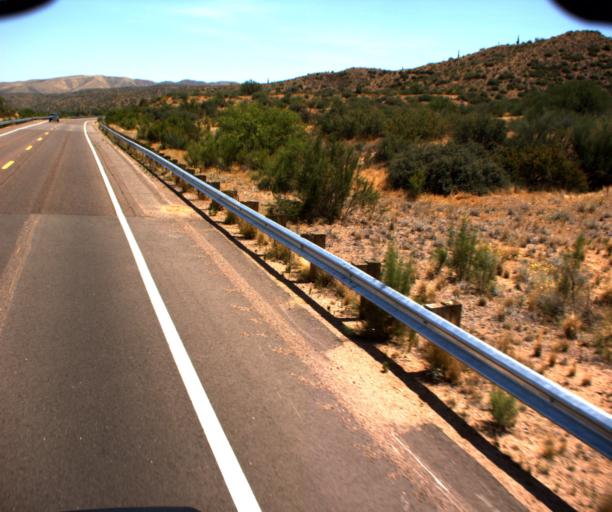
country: US
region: Arizona
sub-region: Gila County
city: Tonto Basin
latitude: 33.7750
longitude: -111.2614
